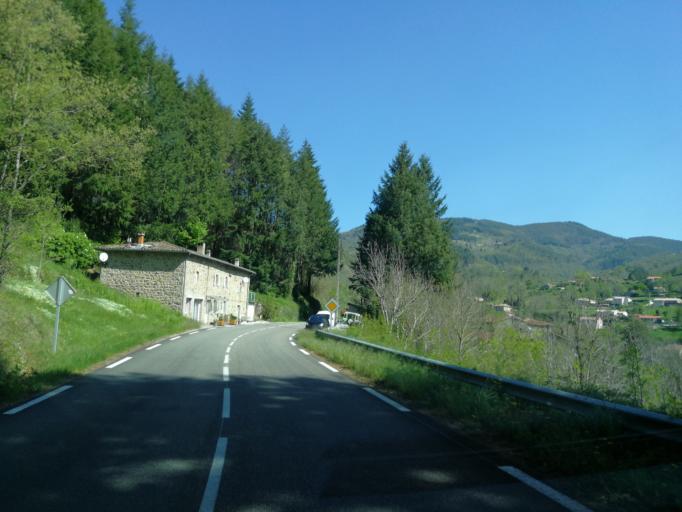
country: FR
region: Rhone-Alpes
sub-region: Departement de l'Ardeche
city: Le Cheylard
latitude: 44.9019
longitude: 4.4840
